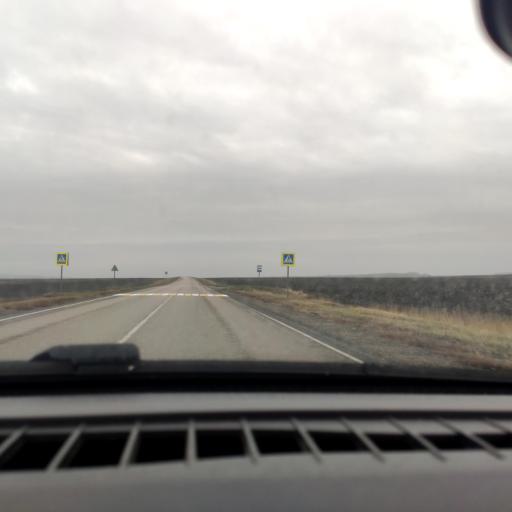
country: RU
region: Belgorod
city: Alekseyevka
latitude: 50.7775
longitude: 38.8176
